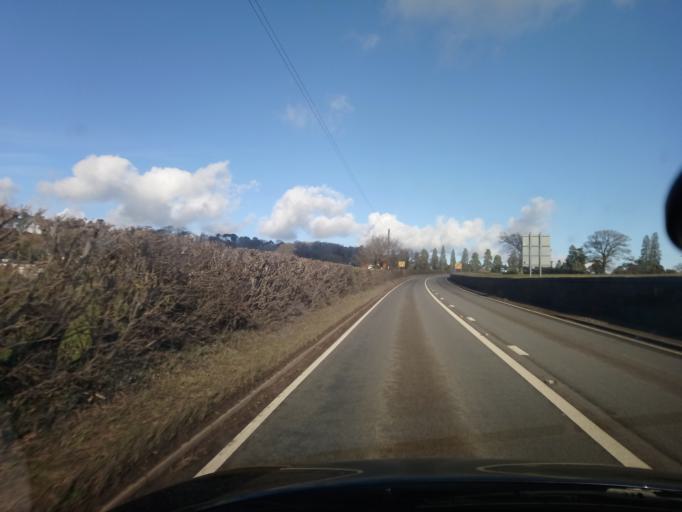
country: GB
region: England
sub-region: Shropshire
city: Clive
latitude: 52.8047
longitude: -2.6991
